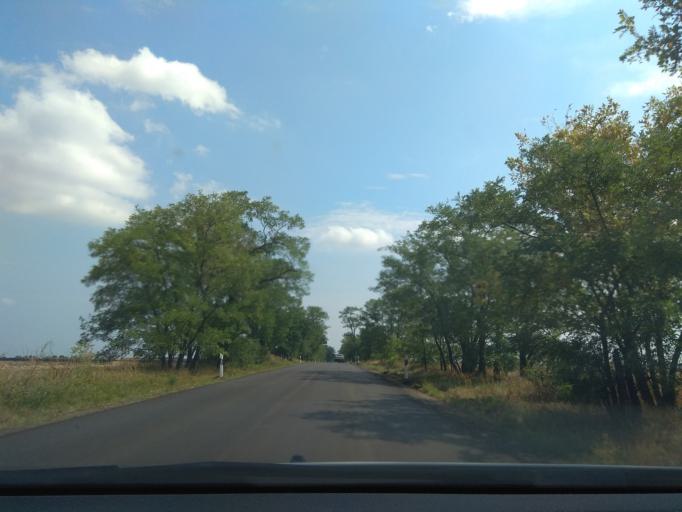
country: HU
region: Heves
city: Szihalom
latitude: 47.8170
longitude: 20.5128
